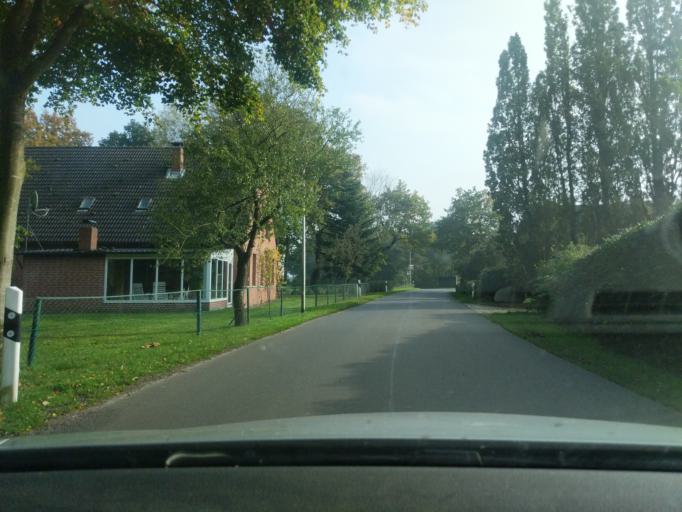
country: DE
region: Lower Saxony
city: Wanna
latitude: 53.7646
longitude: 8.7343
